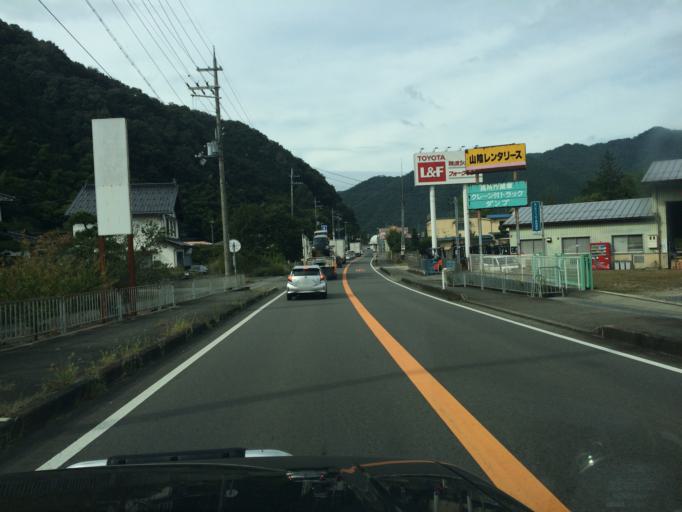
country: JP
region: Hyogo
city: Toyooka
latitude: 35.3495
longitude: 134.8361
